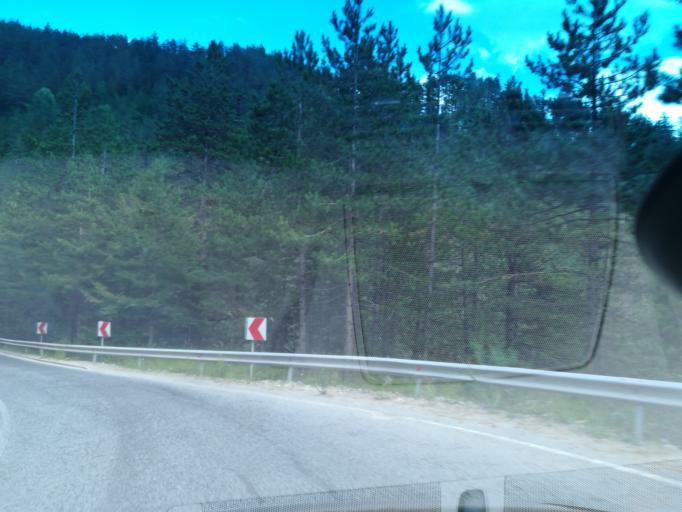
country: BG
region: Smolyan
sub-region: Obshtina Smolyan
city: Smolyan
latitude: 41.6619
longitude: 24.7533
